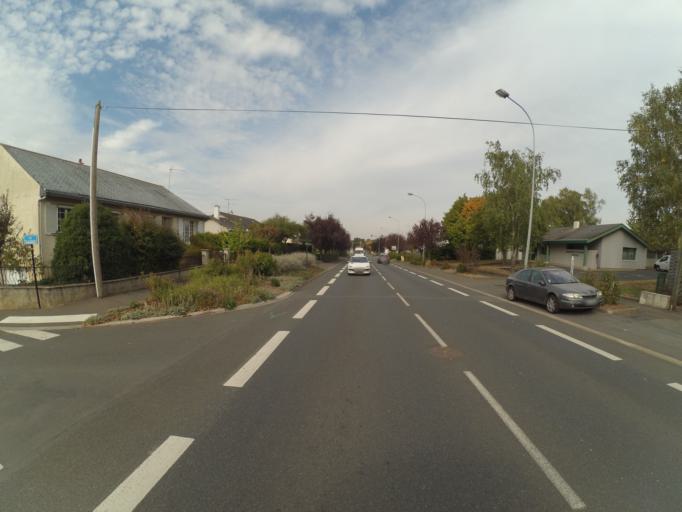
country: FR
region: Pays de la Loire
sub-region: Departement de Maine-et-Loire
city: Chemille-Melay
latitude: 47.2141
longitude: -0.7219
